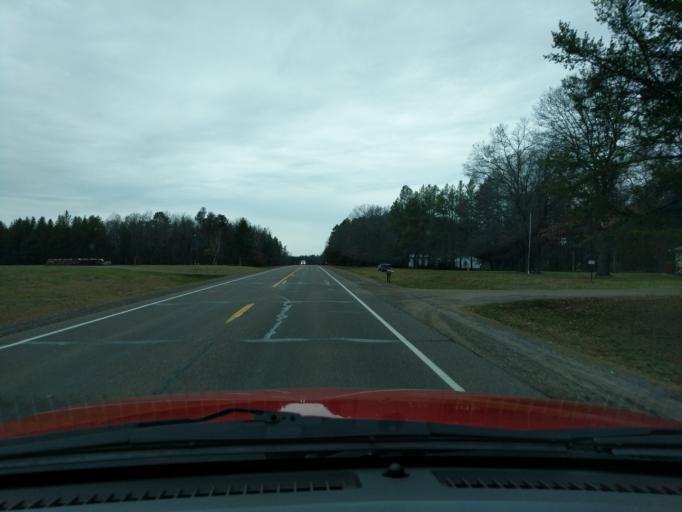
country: US
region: Wisconsin
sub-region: Washburn County
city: Spooner
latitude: 45.8187
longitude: -91.9600
